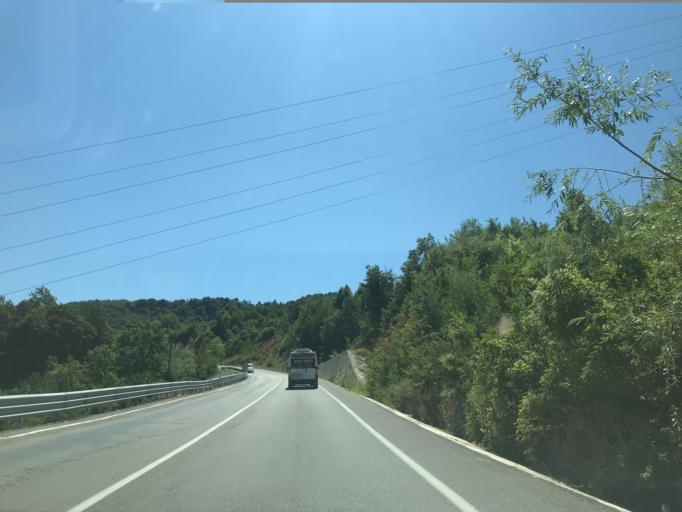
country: TR
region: Bursa
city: Tahtakopru
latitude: 39.9434
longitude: 29.5956
